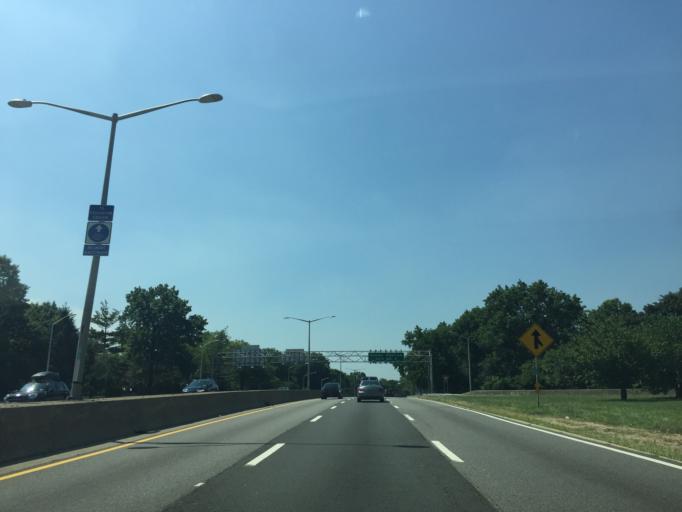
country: US
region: New York
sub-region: Nassau County
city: Bellerose Terrace
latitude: 40.7233
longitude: -73.7250
